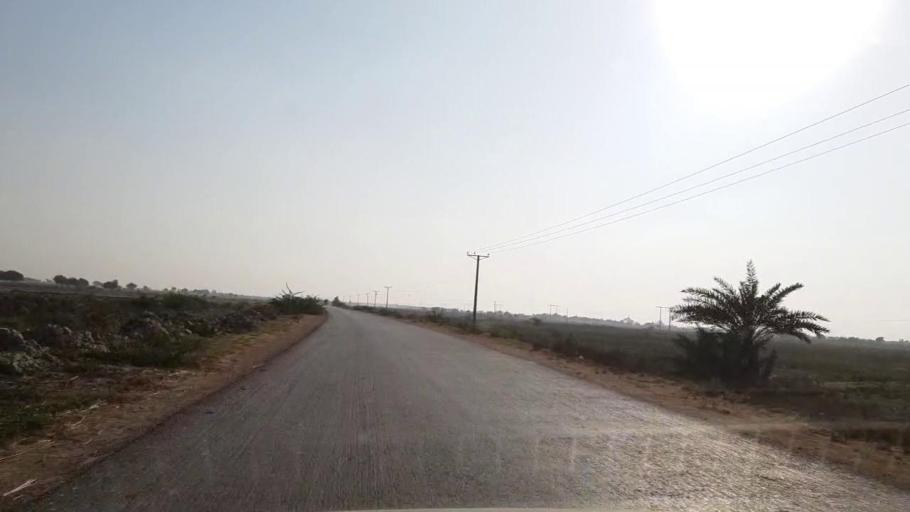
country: PK
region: Sindh
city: Bulri
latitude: 24.9172
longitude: 68.3495
